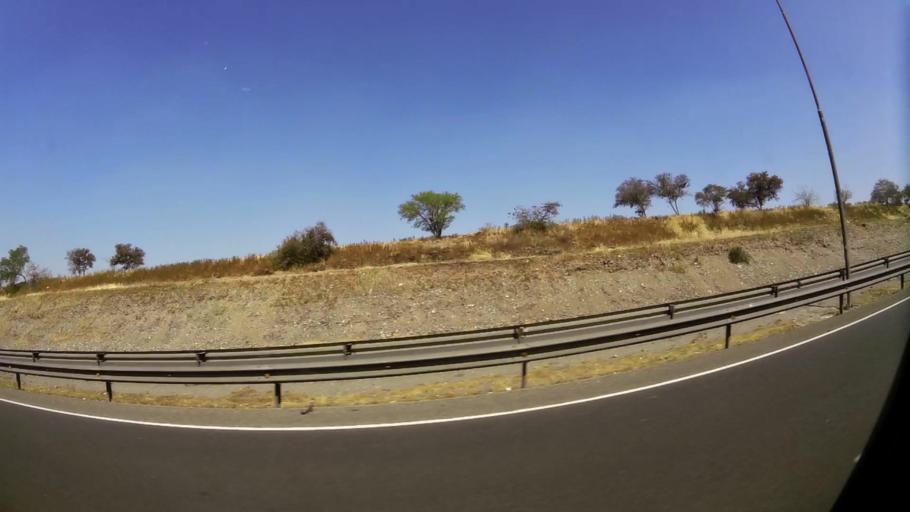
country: CL
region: Santiago Metropolitan
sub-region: Provincia de Santiago
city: Lo Prado
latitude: -33.4838
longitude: -70.7273
